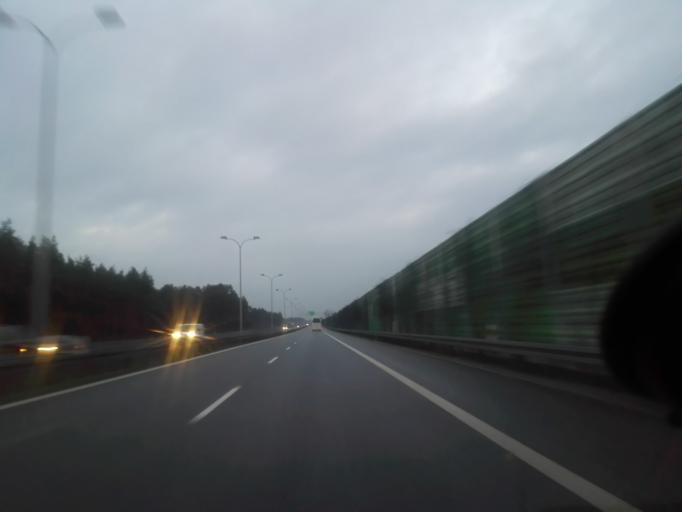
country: PL
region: Masovian Voivodeship
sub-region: Powiat wyszkowski
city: Wyszkow
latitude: 52.5250
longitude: 21.4160
